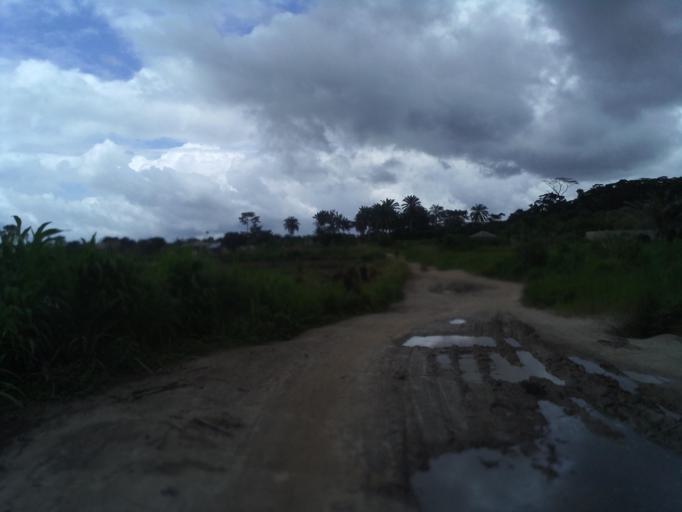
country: SL
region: Eastern Province
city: Kenema
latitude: 7.8360
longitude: -11.1856
